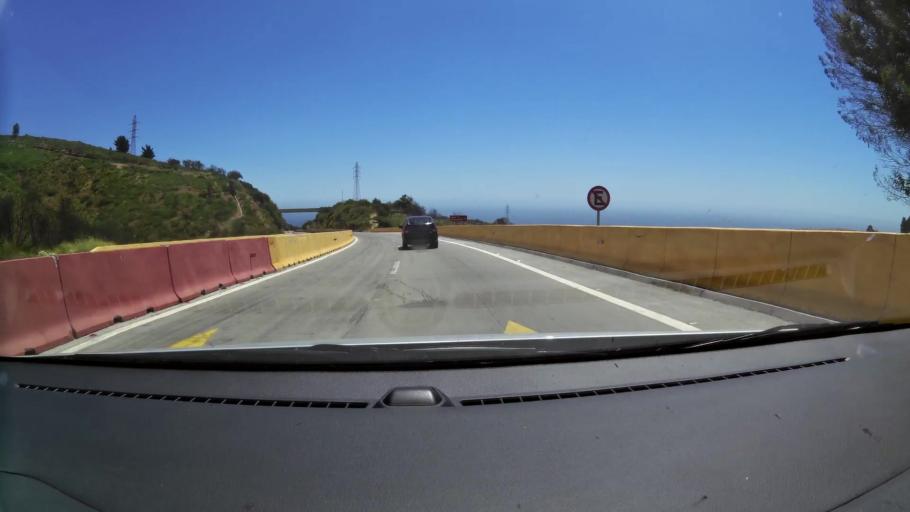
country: CL
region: Valparaiso
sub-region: Provincia de Valparaiso
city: Valparaiso
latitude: -33.0582
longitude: -71.6486
